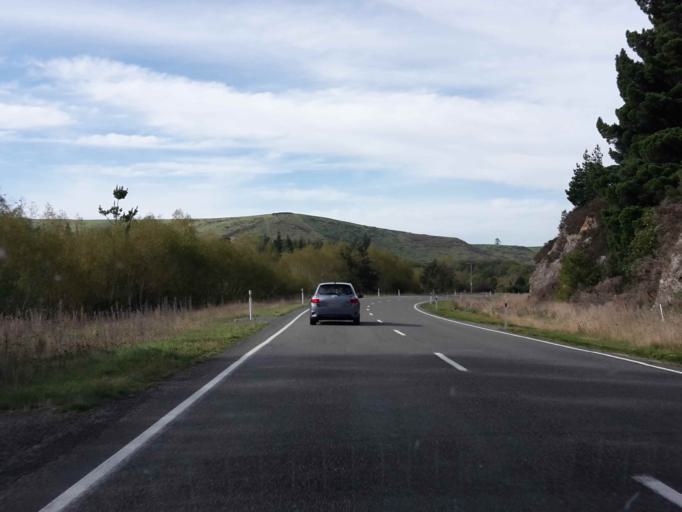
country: NZ
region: Canterbury
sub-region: Timaru District
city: Pleasant Point
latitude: -44.0307
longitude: 170.7103
